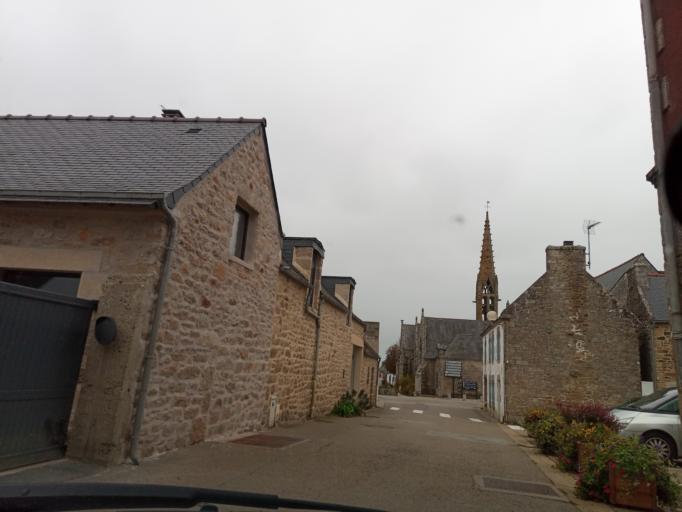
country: FR
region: Brittany
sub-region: Departement du Finistere
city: Esquibien
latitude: 48.0241
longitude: -4.5617
